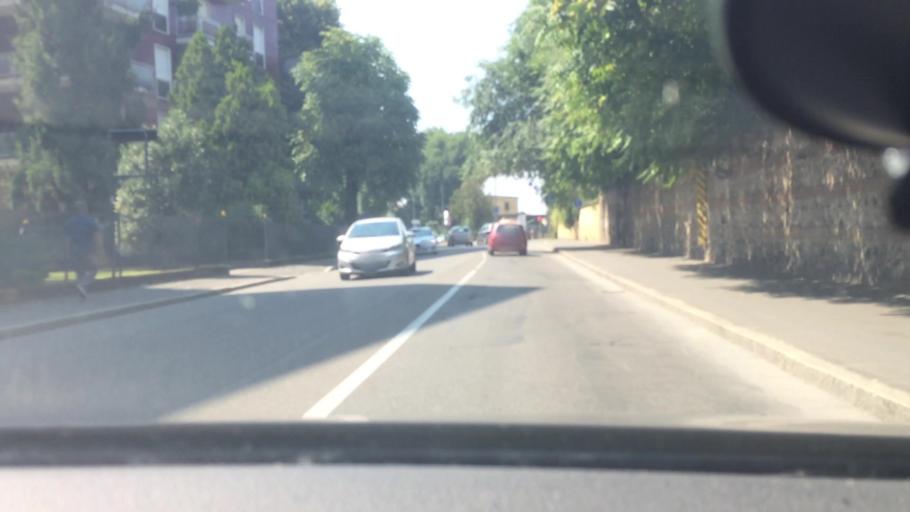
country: IT
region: Emilia-Romagna
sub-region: Provincia di Piacenza
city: Piacenza
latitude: 45.0473
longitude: 9.6843
